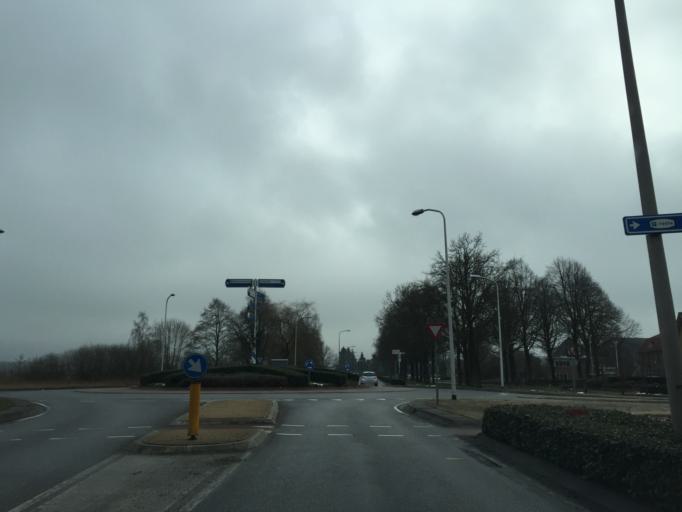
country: NL
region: Overijssel
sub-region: Gemeente Dalfsen
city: Dalfsen
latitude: 52.5078
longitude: 6.2632
